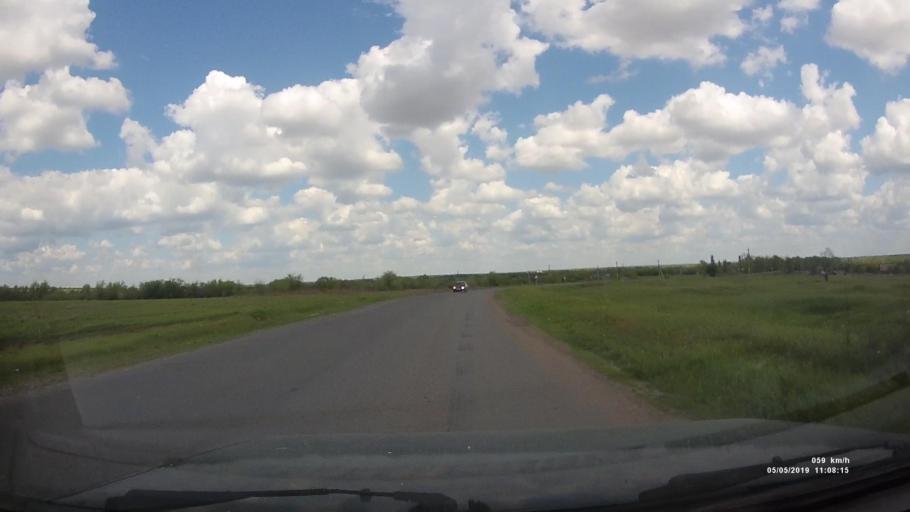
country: RU
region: Rostov
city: Ust'-Donetskiy
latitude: 47.7314
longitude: 40.9148
